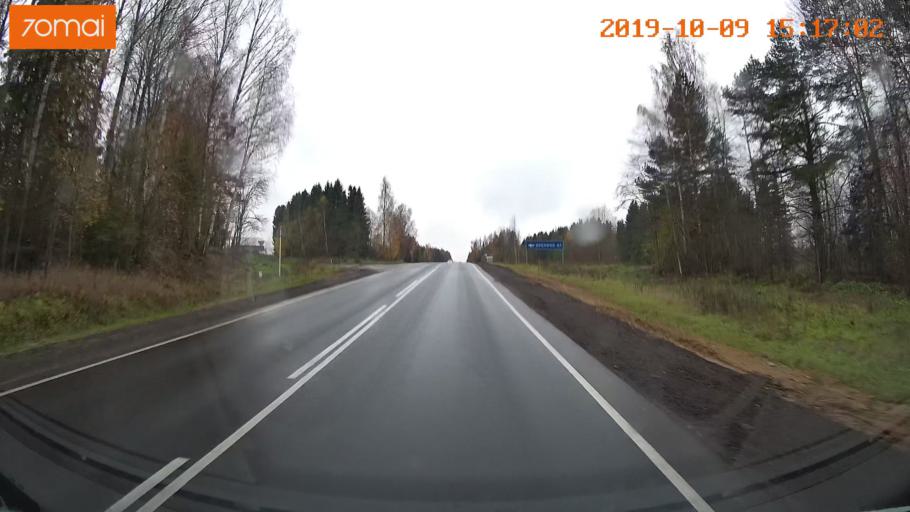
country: RU
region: Kostroma
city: Susanino
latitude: 58.1036
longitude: 41.5842
